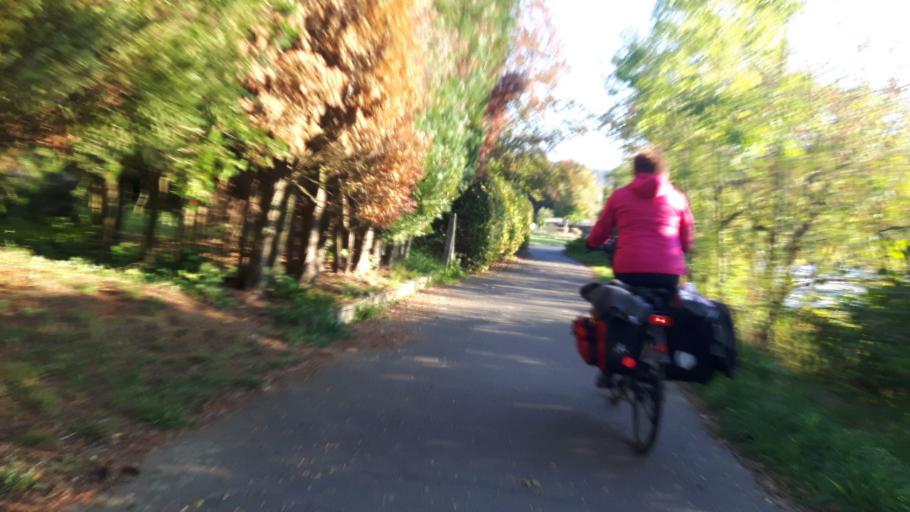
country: DE
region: Rheinland-Pfalz
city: Niederirsen
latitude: 50.8069
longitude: 7.5567
